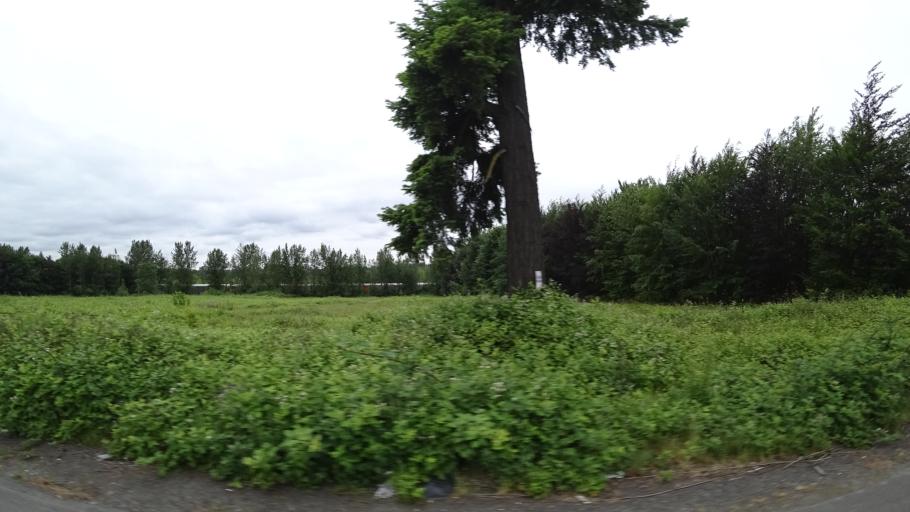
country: US
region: Oregon
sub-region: Multnomah County
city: Fairview
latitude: 45.5475
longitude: -122.4852
